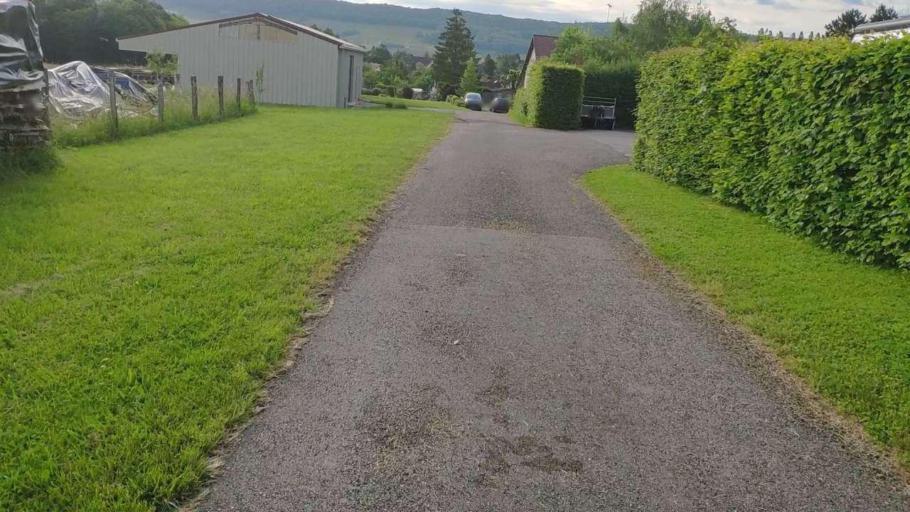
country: FR
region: Franche-Comte
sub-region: Departement du Jura
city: Perrigny
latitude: 46.7316
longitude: 5.5765
